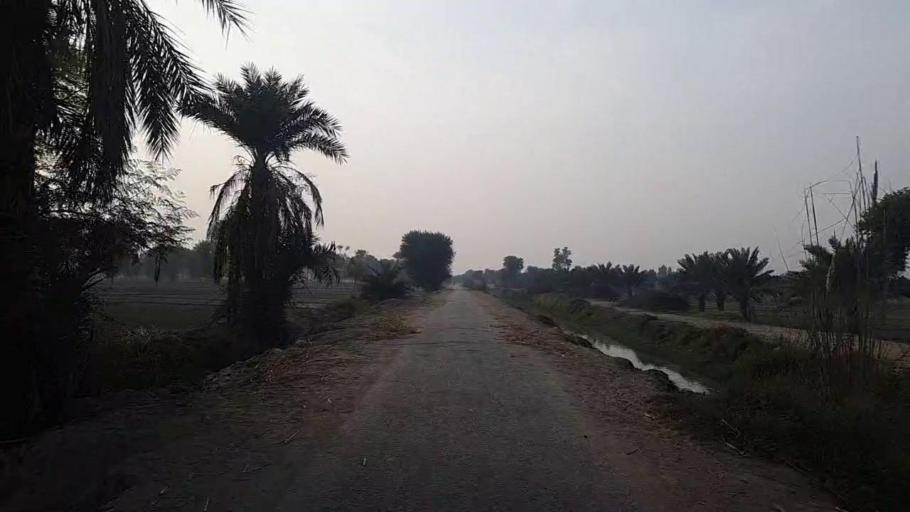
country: PK
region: Sindh
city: Kot Diji
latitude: 27.3743
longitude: 68.6547
